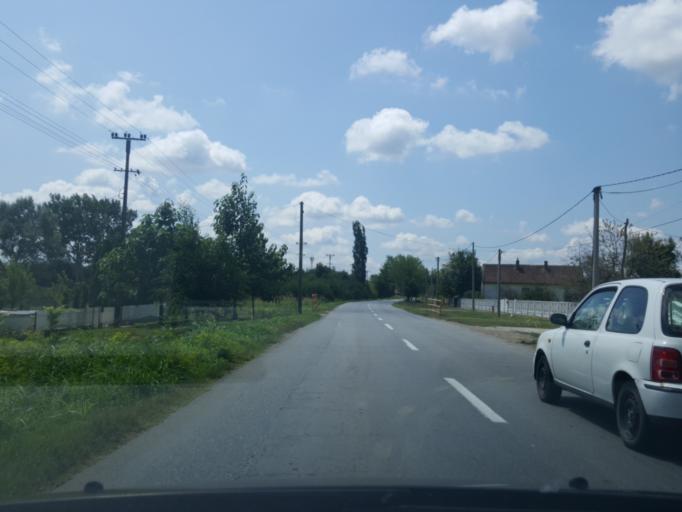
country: RS
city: Salas Nocajski
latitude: 44.9353
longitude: 19.5709
